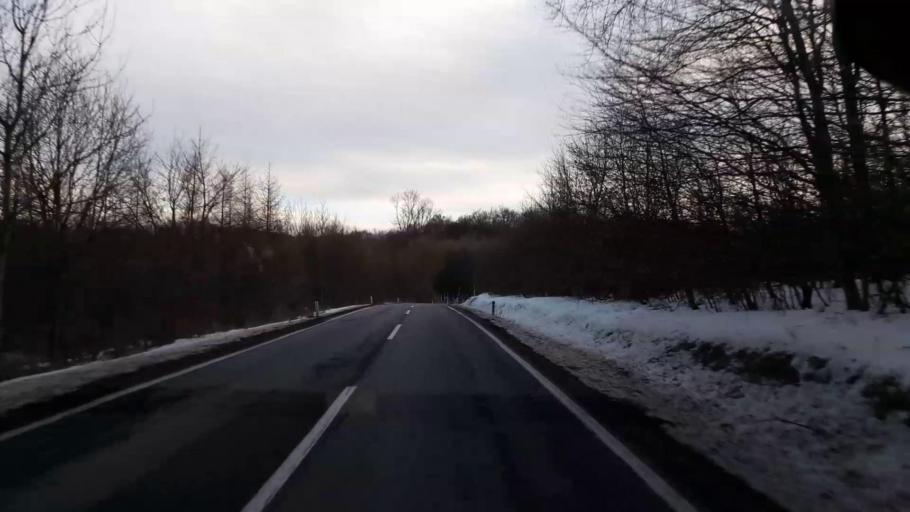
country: AT
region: Lower Austria
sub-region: Politischer Bezirk Wien-Umgebung
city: Mauerbach
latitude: 48.2720
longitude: 16.1916
